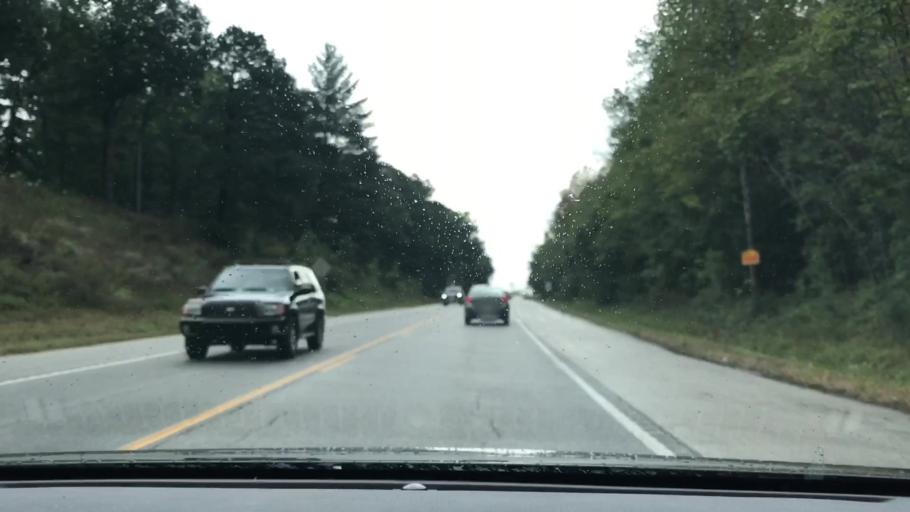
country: US
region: Tennessee
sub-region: Macon County
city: Red Boiling Springs
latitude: 36.5235
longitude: -85.8800
